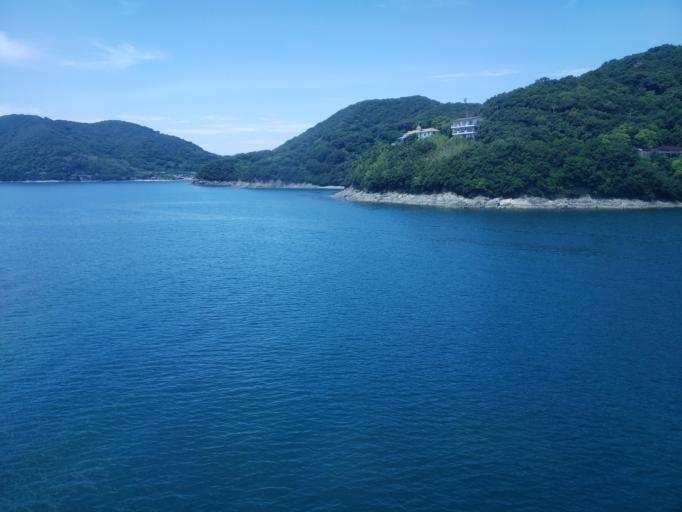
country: JP
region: Kagawa
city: Tonosho
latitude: 34.4530
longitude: 134.3157
